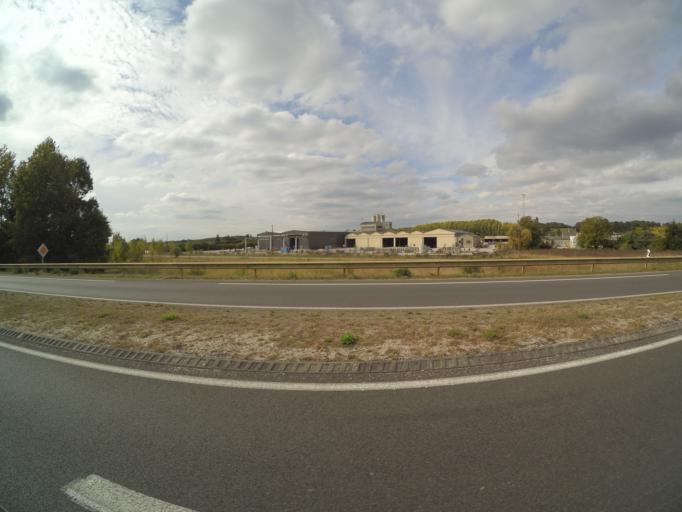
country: FR
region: Centre
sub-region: Departement d'Indre-et-Loire
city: Cinq-Mars-la-Pile
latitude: 47.3421
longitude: 0.4654
